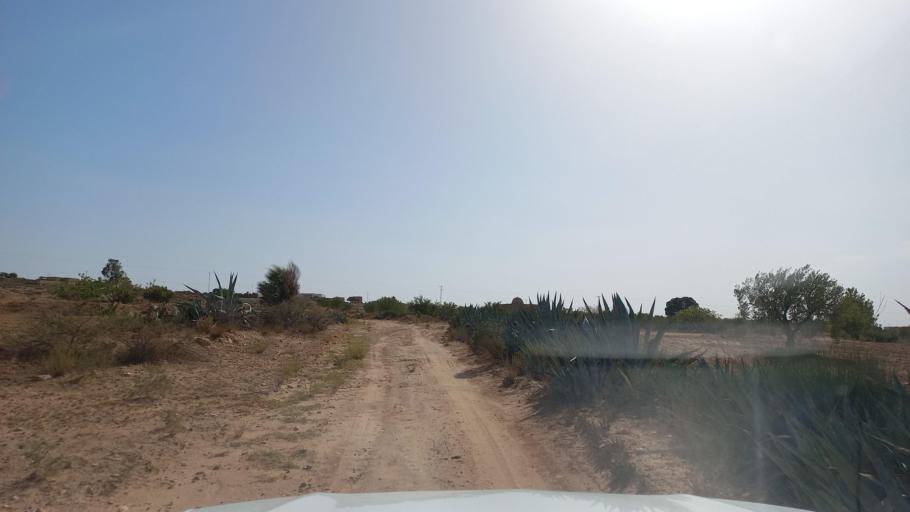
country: TN
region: Al Qasrayn
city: Kasserine
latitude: 35.2091
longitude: 8.9762
